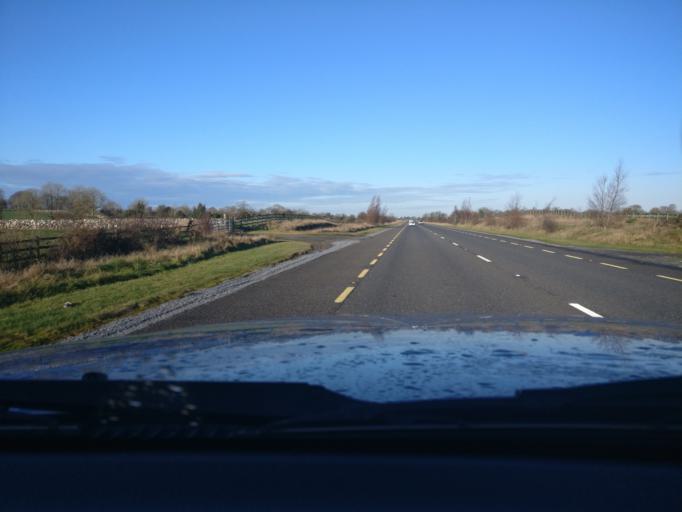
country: IE
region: Connaught
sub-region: County Galway
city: Loughrea
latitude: 53.2202
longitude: -8.5811
